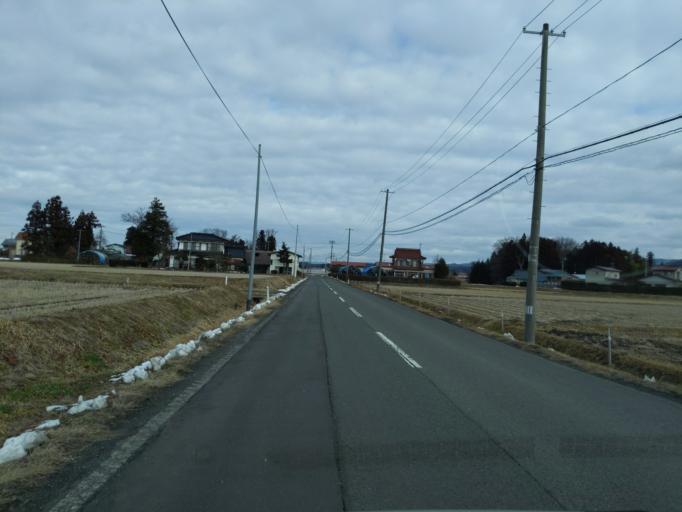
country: JP
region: Iwate
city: Mizusawa
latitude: 39.0761
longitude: 141.1637
